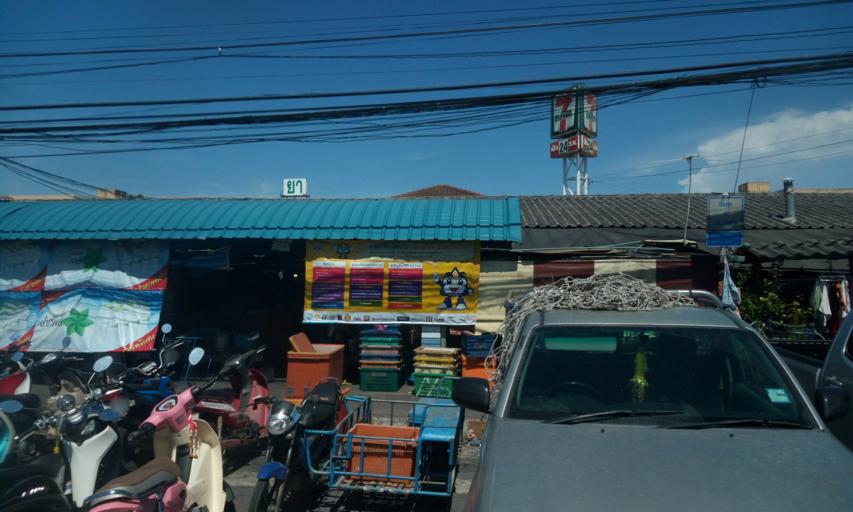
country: TH
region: Samut Prakan
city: Bang Bo District
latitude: 13.5603
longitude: 100.7657
